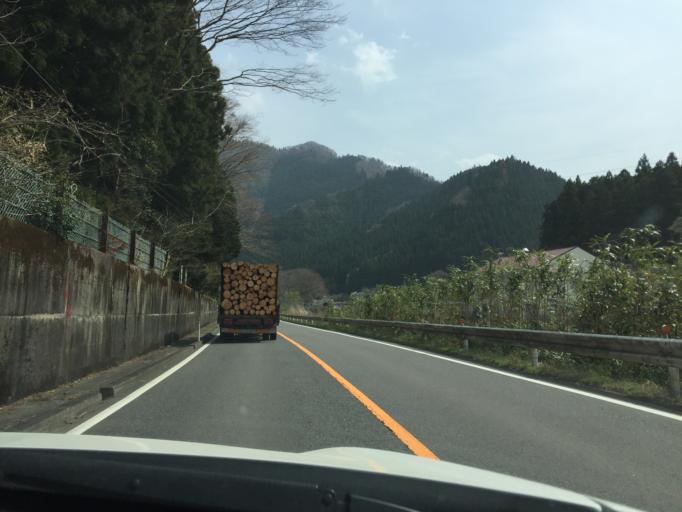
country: JP
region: Fukushima
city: Ishikawa
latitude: 37.0385
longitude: 140.6215
